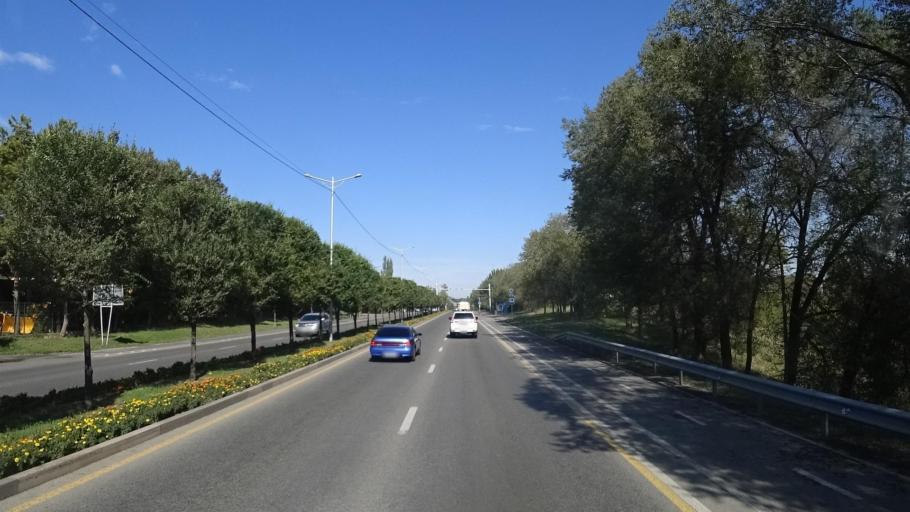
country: KZ
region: Almaty Oblysy
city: Pervomayskiy
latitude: 43.3360
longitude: 77.0026
